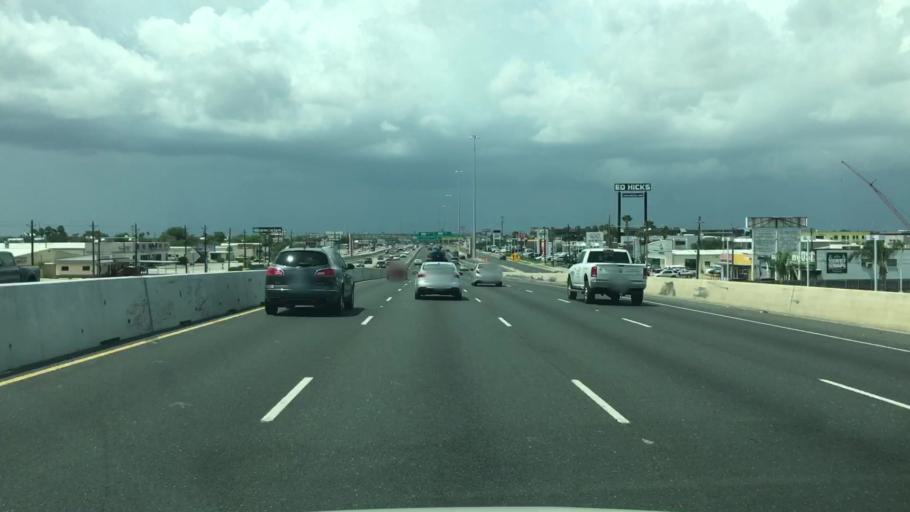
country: US
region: Texas
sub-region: Nueces County
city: Corpus Christi
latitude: 27.7291
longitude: -97.4138
